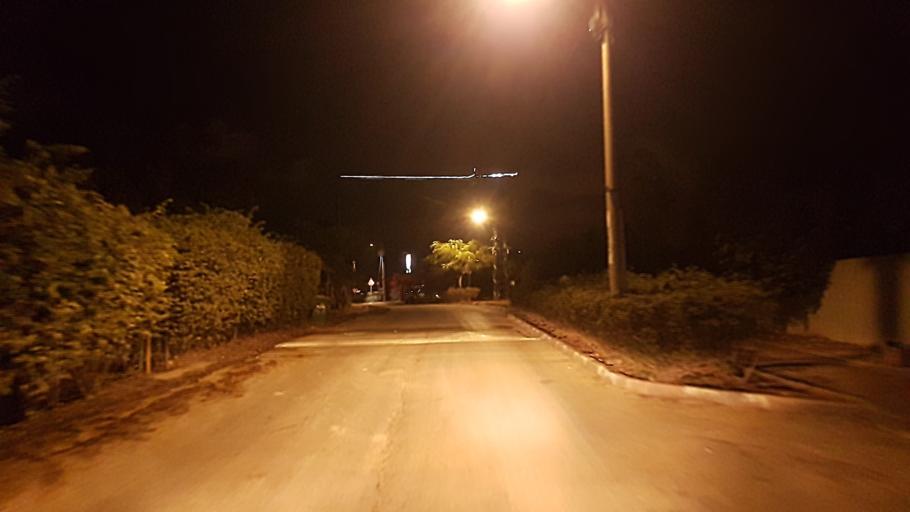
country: IL
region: Central District
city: Hod HaSharon
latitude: 32.1469
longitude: 34.8962
